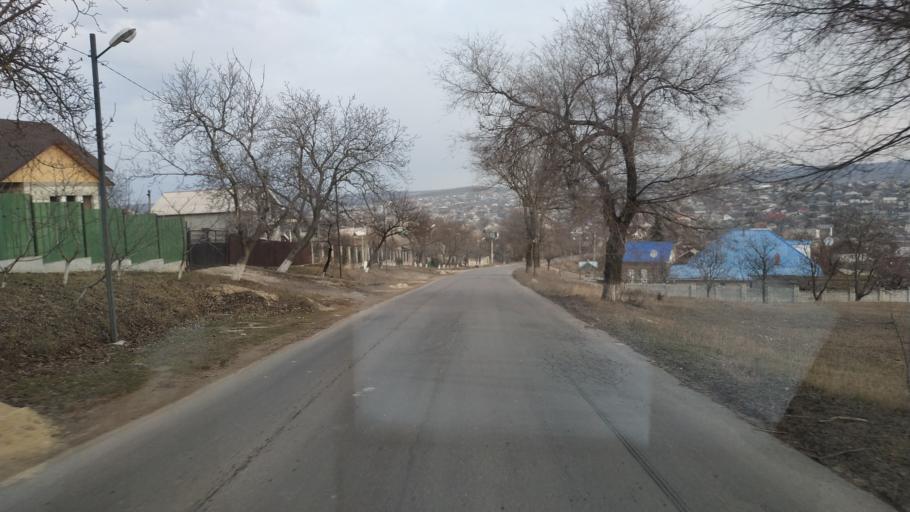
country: MD
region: Chisinau
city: Singera
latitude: 46.9537
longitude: 29.0577
